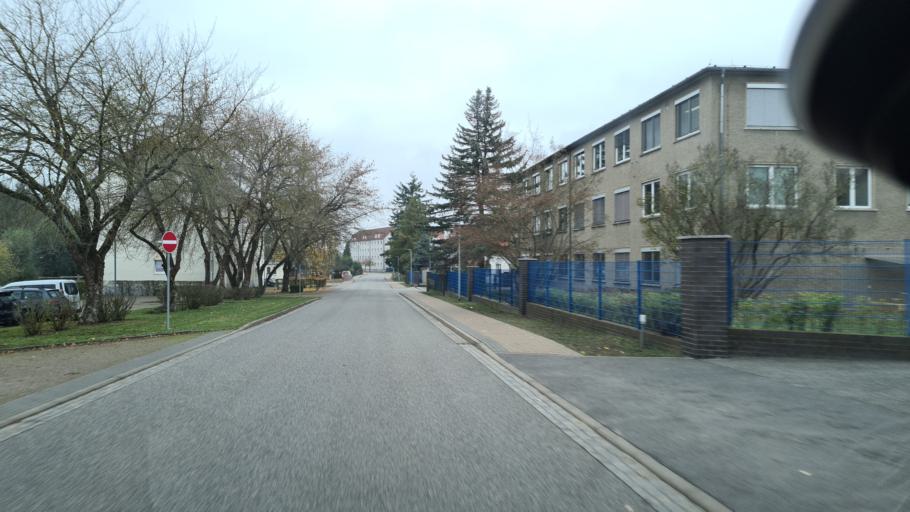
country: DE
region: Brandenburg
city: Lindow
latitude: 52.9644
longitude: 12.9904
